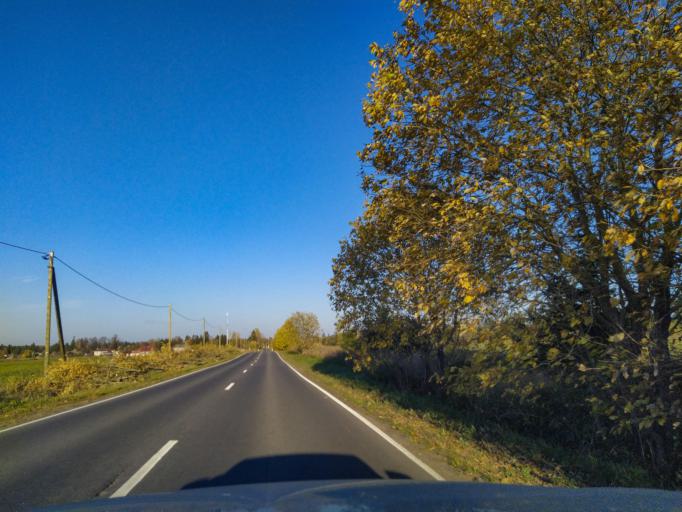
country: RU
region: Leningrad
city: Siverskiy
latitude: 59.3311
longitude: 30.0471
